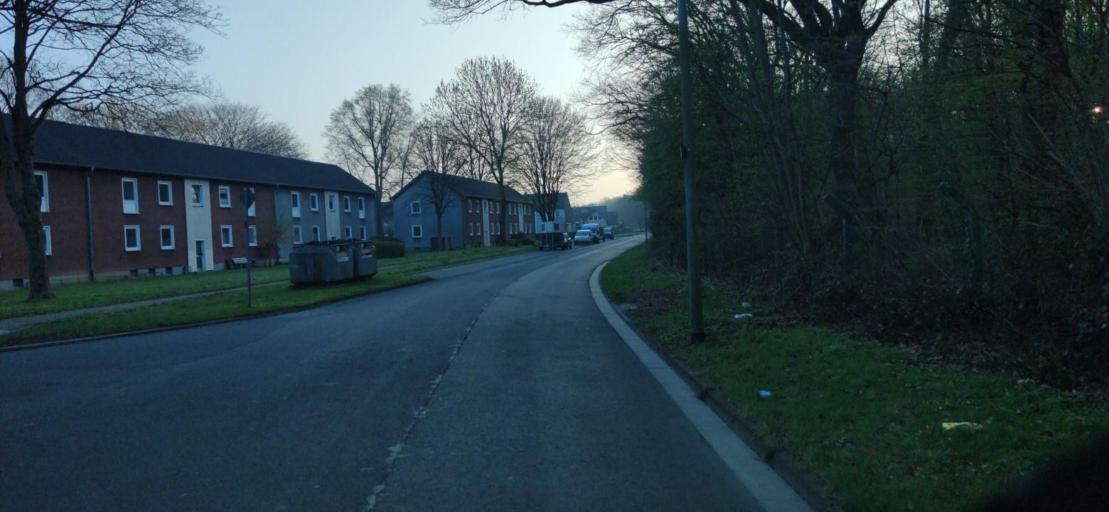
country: DE
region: North Rhine-Westphalia
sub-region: Regierungsbezirk Dusseldorf
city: Voerde
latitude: 51.5776
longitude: 6.6969
